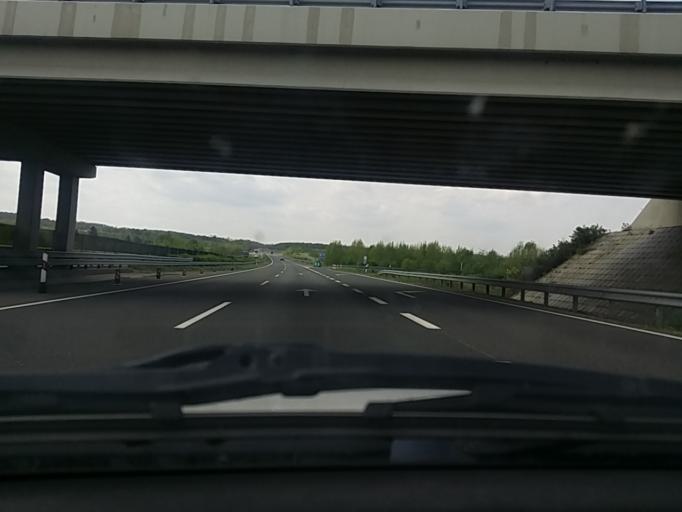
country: HU
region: Somogy
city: Balatonszarszo
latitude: 46.8037
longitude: 17.8138
